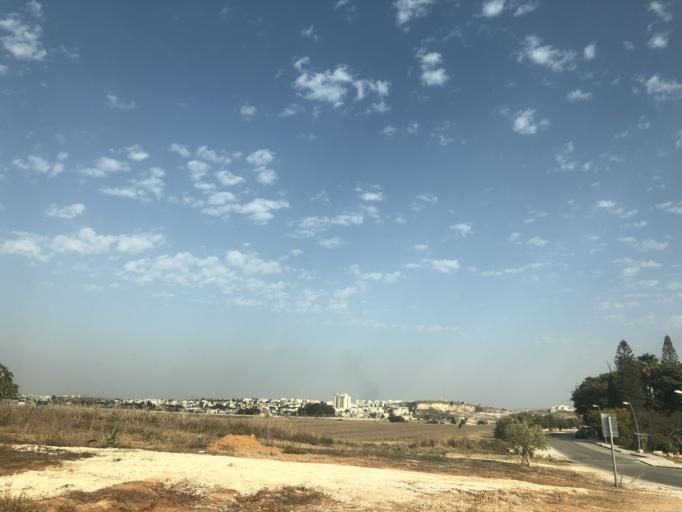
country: IL
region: Central District
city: Rosh Ha'Ayin
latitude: 32.0859
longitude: 34.9380
